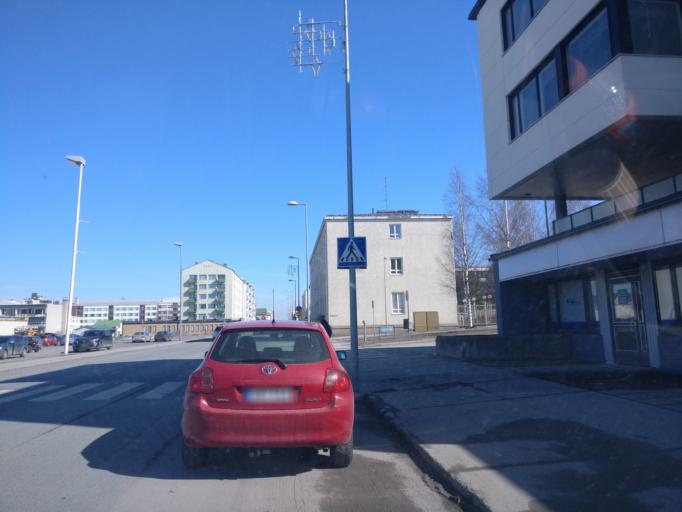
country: FI
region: Lapland
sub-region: Kemi-Tornio
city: Kemi
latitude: 65.7345
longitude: 24.5592
